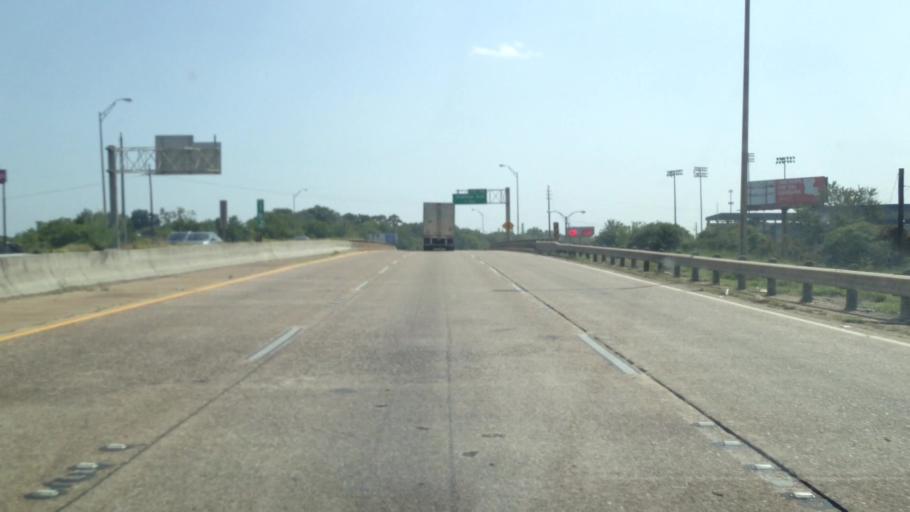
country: US
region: Louisiana
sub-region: Caddo Parish
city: Shreveport
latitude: 32.4796
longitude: -93.7792
